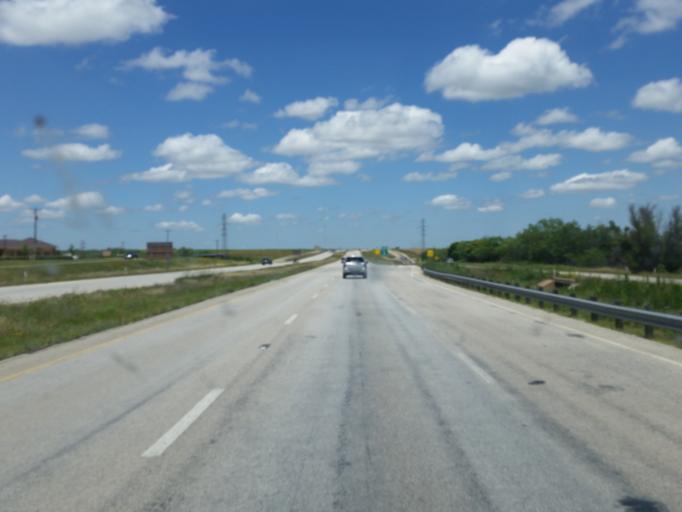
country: US
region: Texas
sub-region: Nolan County
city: Sweetwater
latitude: 32.4604
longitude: -100.3854
